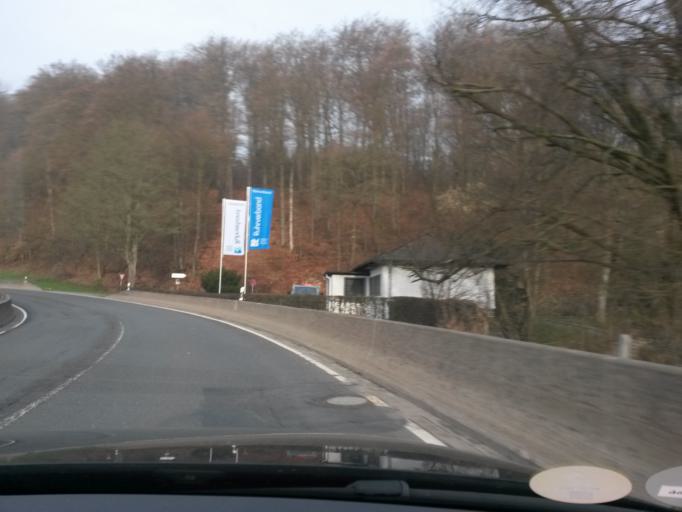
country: DE
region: North Rhine-Westphalia
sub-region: Regierungsbezirk Arnsberg
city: Herscheid
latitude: 51.1932
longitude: 7.6839
